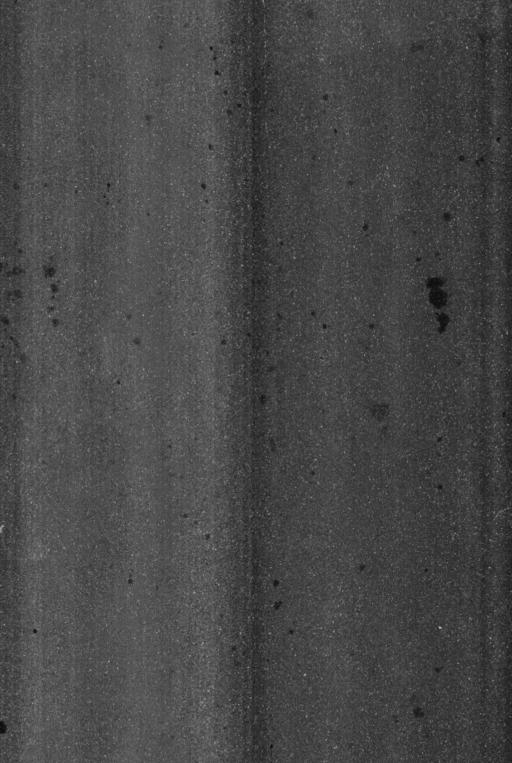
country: US
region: Maryland
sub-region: Prince George's County
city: Mount Rainier
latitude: 38.9250
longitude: -76.9636
